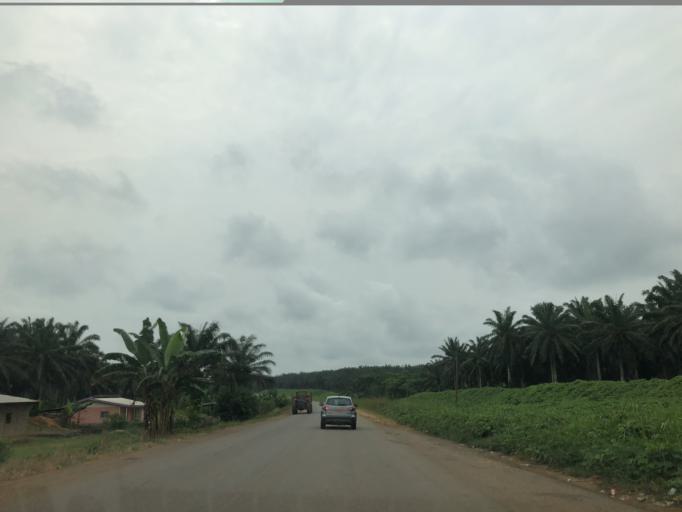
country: CM
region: Littoral
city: Edea
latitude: 3.5774
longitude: 10.1094
